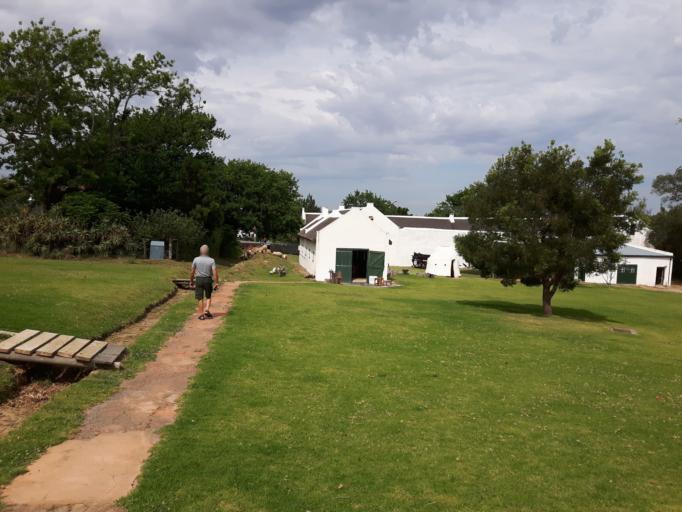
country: ZA
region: Western Cape
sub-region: Overberg District Municipality
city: Swellendam
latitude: -34.0180
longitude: 20.4535
